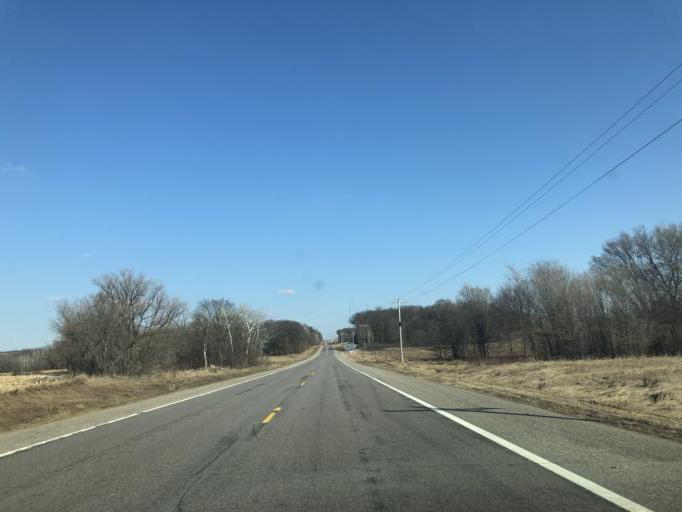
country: US
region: Minnesota
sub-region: Sherburne County
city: Becker
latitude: 45.4298
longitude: -93.8556
